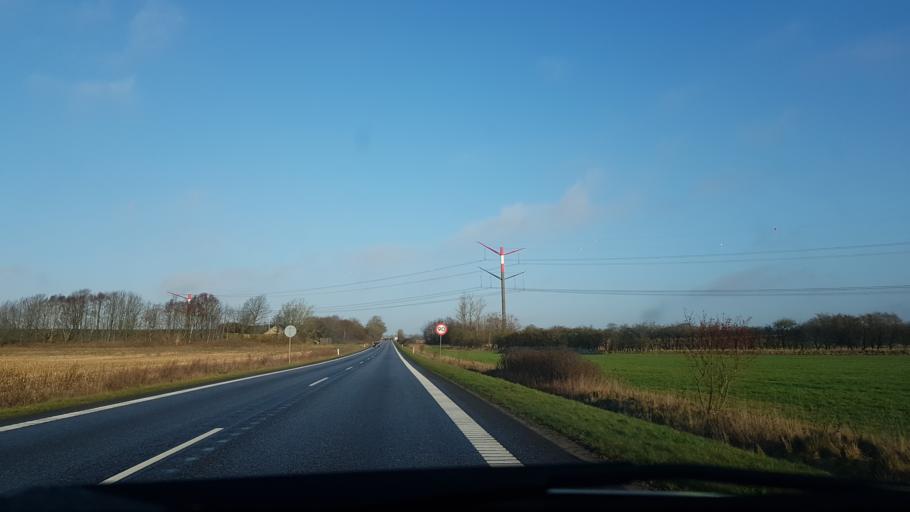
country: DK
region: South Denmark
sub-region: Tonder Kommune
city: Toftlund
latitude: 55.2473
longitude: 9.1380
